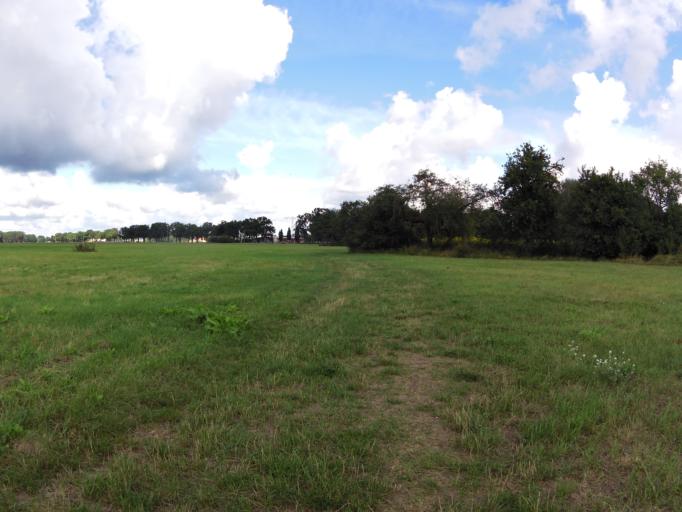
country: DE
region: Brandenburg
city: Storkow
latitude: 52.2621
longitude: 13.9342
